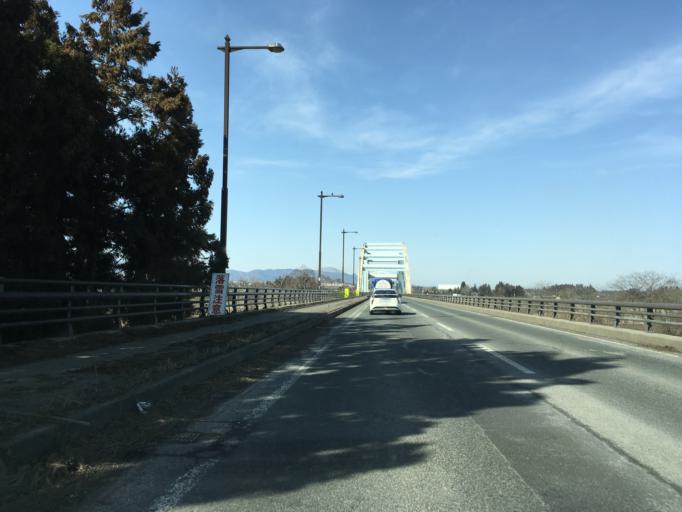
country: JP
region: Iwate
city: Hanamaki
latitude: 39.3987
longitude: 141.1411
